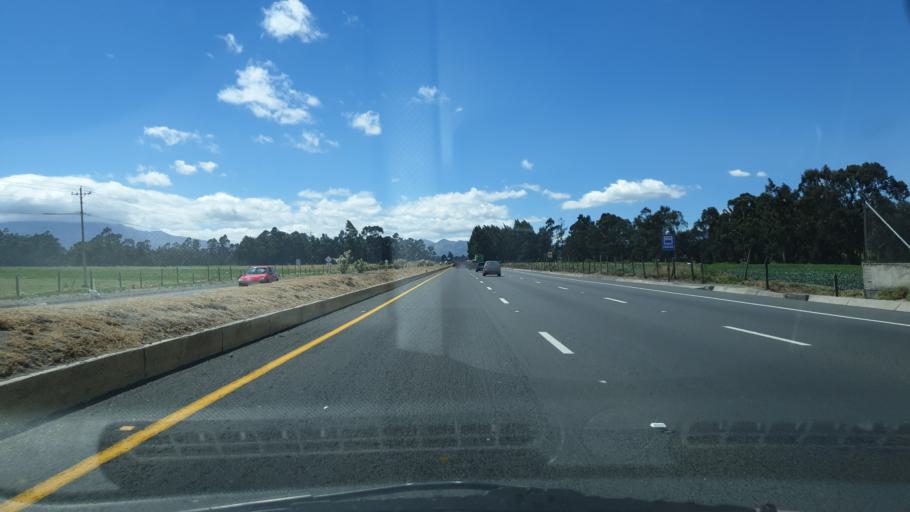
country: EC
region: Cotopaxi
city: Saquisili
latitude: -0.8445
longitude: -78.6193
